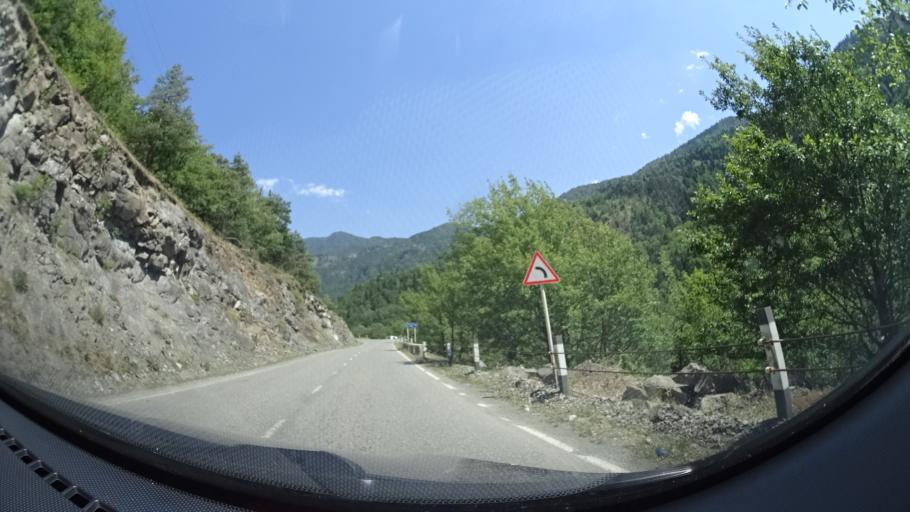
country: GE
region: Ajaria
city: Khulo
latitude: 41.6252
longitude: 42.2832
